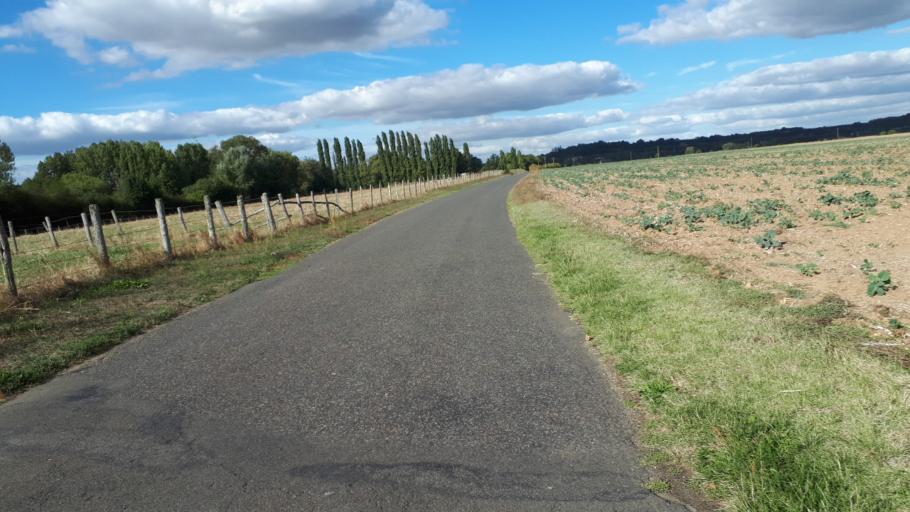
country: FR
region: Centre
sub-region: Departement du Loir-et-Cher
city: Villiers-sur-Loir
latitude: 47.7975
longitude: 0.9571
